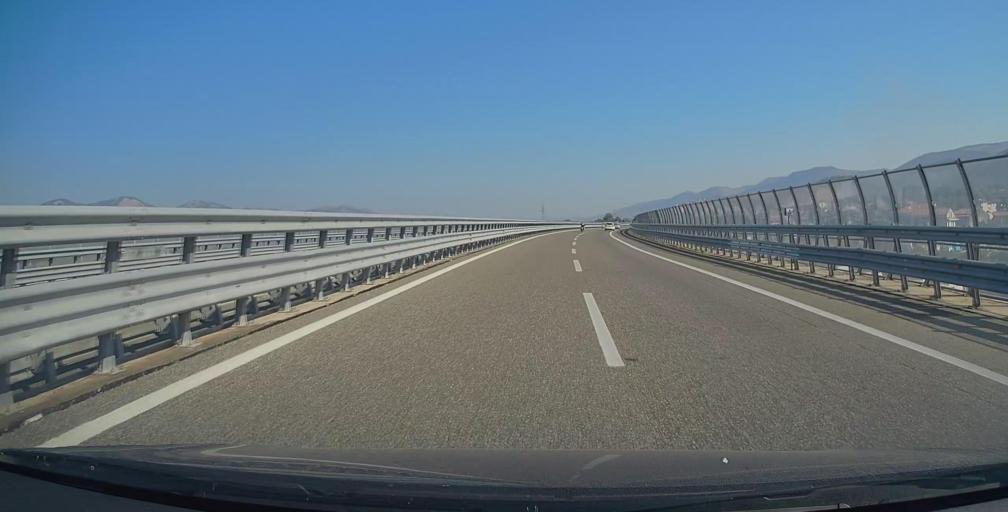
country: IT
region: Campania
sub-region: Provincia di Salerno
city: Atena Lucana
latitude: 40.4144
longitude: 15.5617
